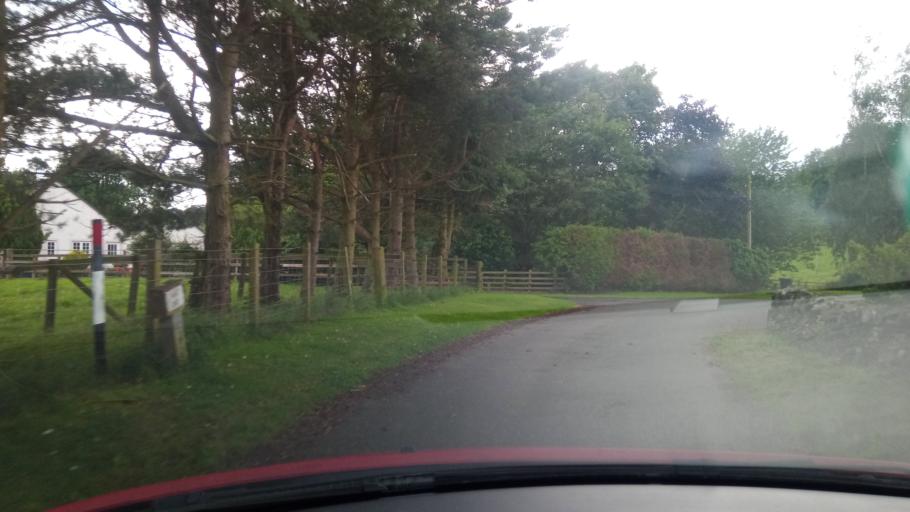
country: GB
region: Scotland
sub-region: The Scottish Borders
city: Hawick
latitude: 55.4254
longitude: -2.7499
